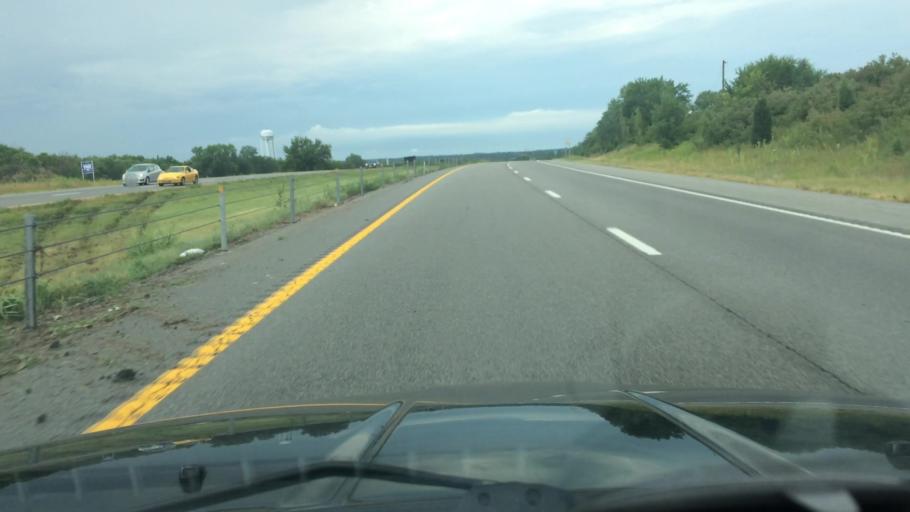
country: US
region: Missouri
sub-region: Cass County
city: Peculiar
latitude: 38.7465
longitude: -94.4767
